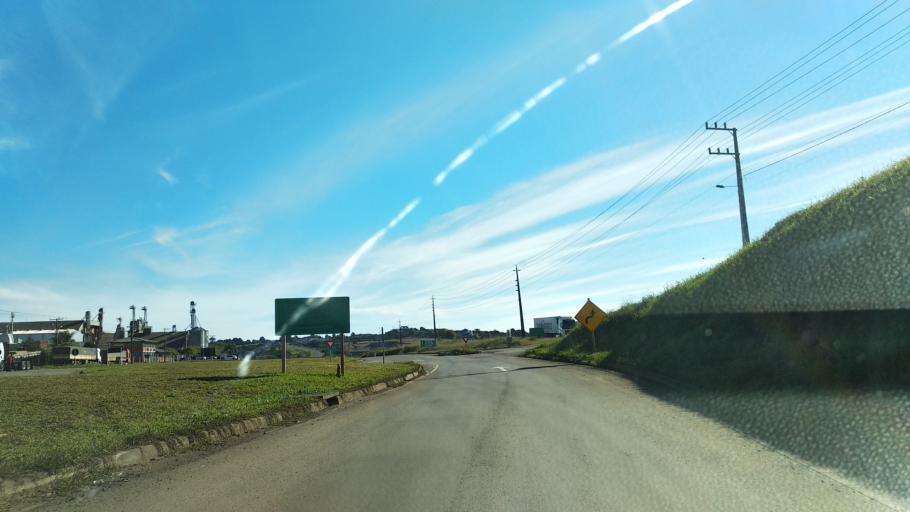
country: BR
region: Santa Catarina
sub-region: Campos Novos
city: Campos Novos
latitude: -27.4083
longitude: -51.2136
